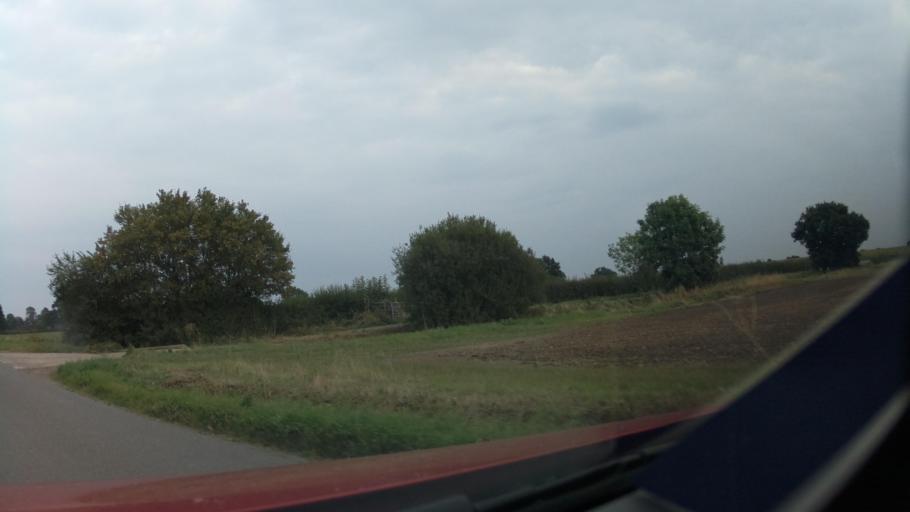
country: GB
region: England
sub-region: Lincolnshire
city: Skellingthorpe
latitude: 53.1430
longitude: -0.6564
